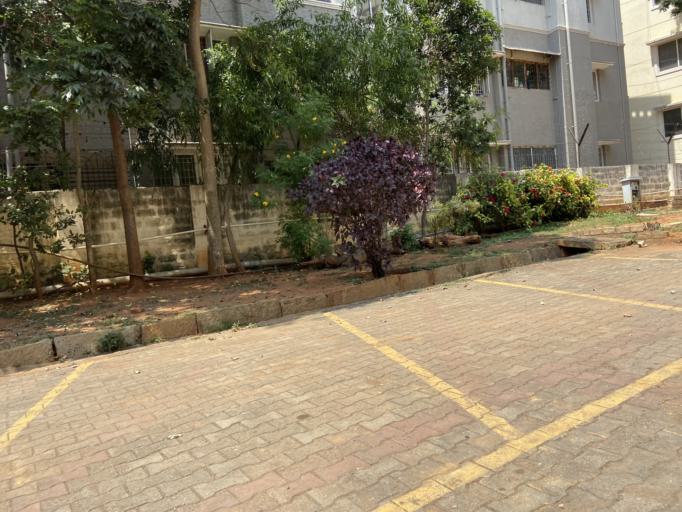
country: IN
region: Karnataka
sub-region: Bangalore Urban
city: Bangalore
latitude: 12.9531
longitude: 77.6491
